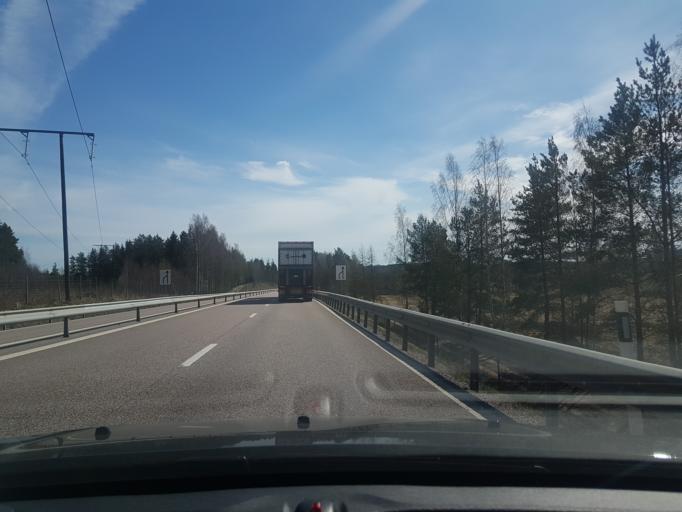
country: SE
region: Dalarna
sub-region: Hedemora Kommun
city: Brunna
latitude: 60.2460
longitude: 16.0228
